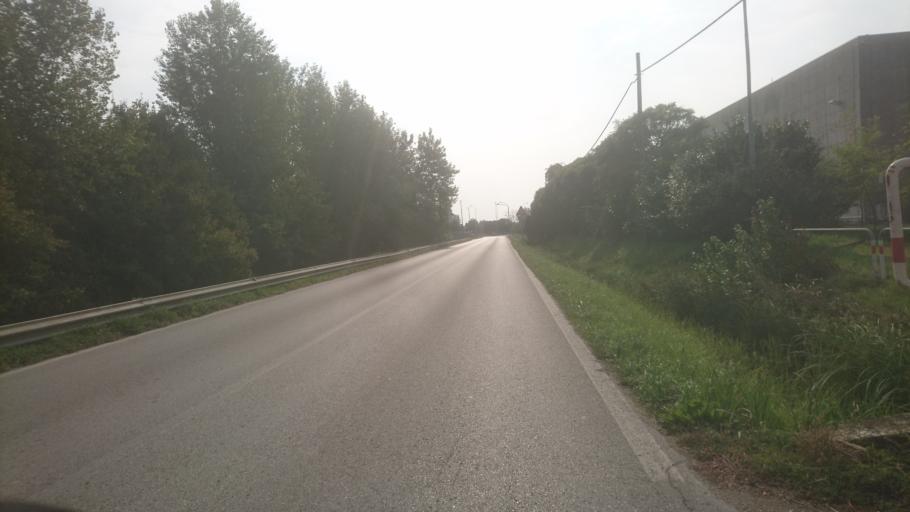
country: IT
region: Veneto
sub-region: Provincia di Vicenza
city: Quinto Vicentino
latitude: 45.5768
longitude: 11.6457
